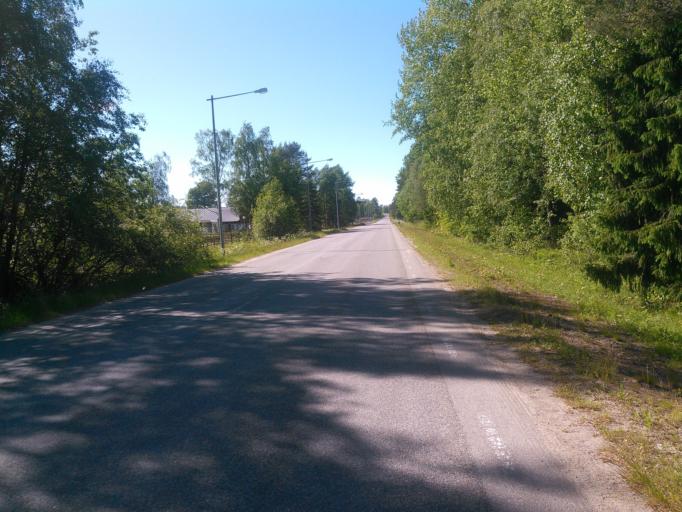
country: SE
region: Vaesterbotten
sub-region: Umea Kommun
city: Roback
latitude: 63.8221
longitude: 20.1879
